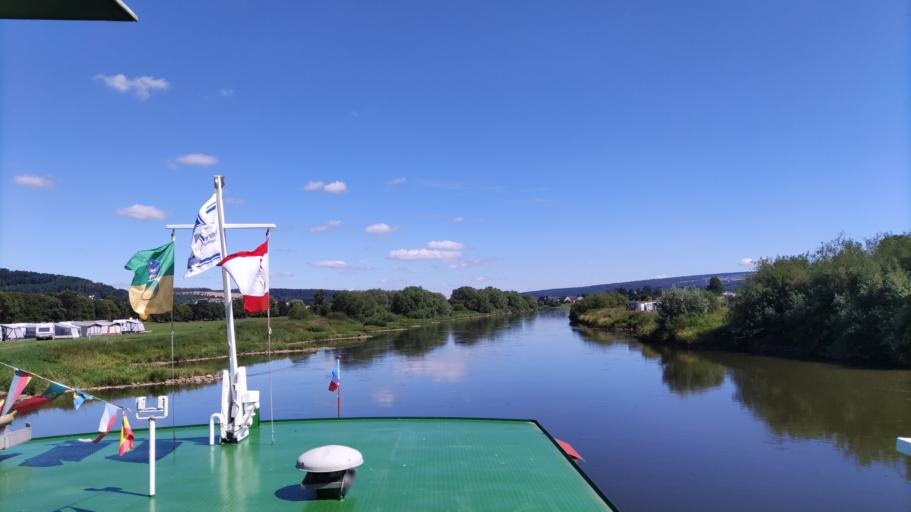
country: DE
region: North Rhine-Westphalia
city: Beverungen
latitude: 51.6502
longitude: 9.3746
